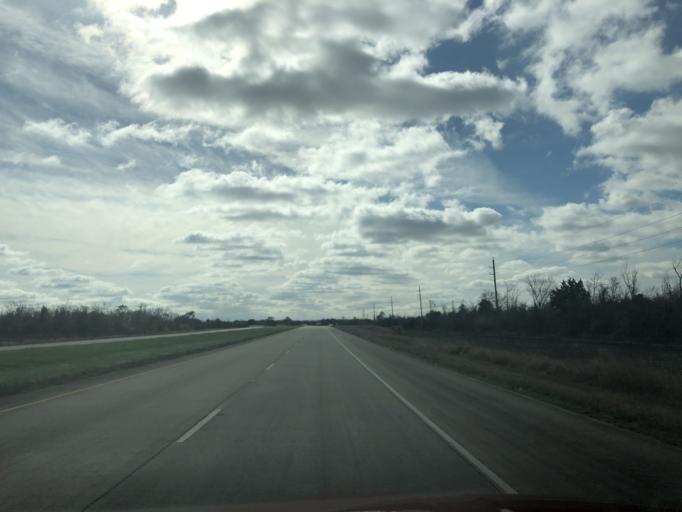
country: US
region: Texas
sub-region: Chambers County
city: Beach City
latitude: 29.7440
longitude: -94.8732
